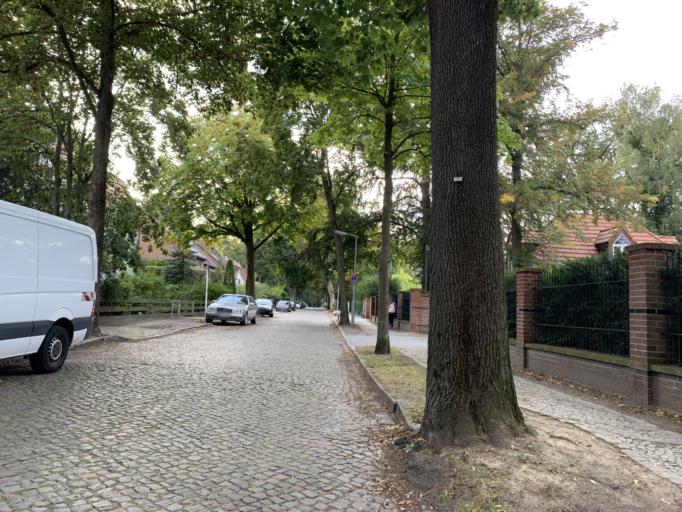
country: DE
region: Berlin
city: Wannsee
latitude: 52.4143
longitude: 13.1613
